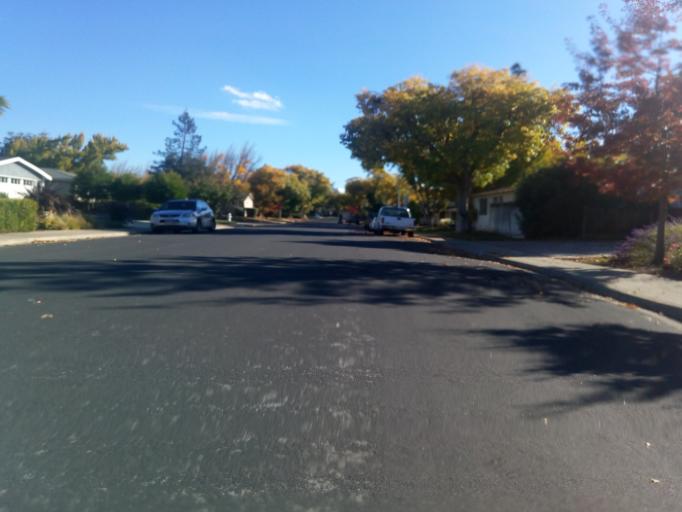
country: US
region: California
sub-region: Santa Clara County
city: Mountain View
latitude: 37.3766
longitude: -122.0841
